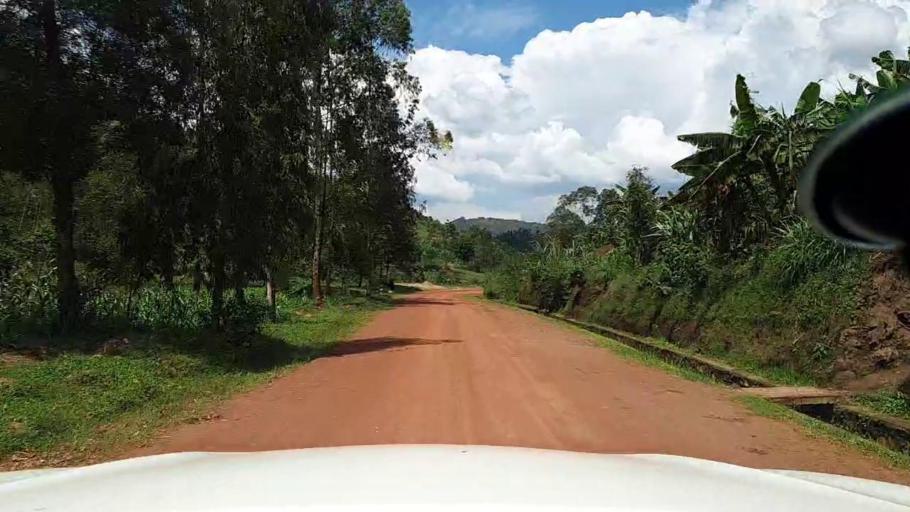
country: RW
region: Northern Province
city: Byumba
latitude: -1.7001
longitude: 29.8316
